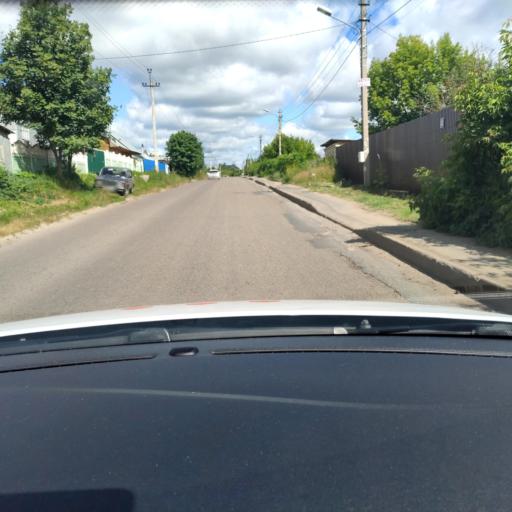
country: RU
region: Tatarstan
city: Vysokaya Gora
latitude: 55.8621
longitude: 49.2387
